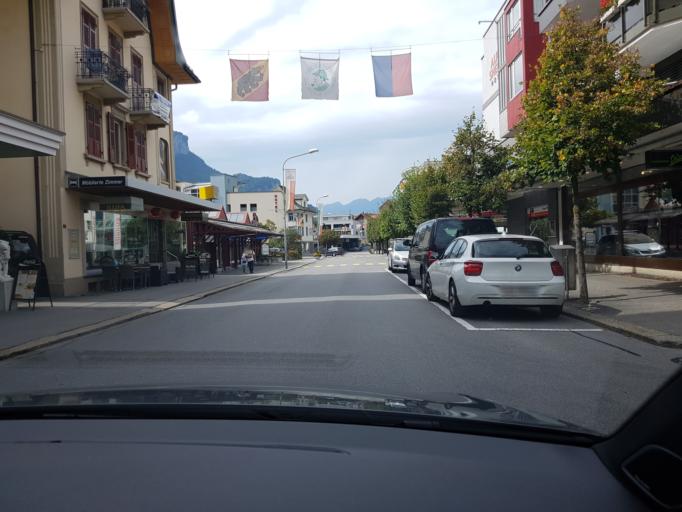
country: CH
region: Bern
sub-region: Interlaken-Oberhasli District
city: Meiringen
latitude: 46.7279
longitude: 8.1860
